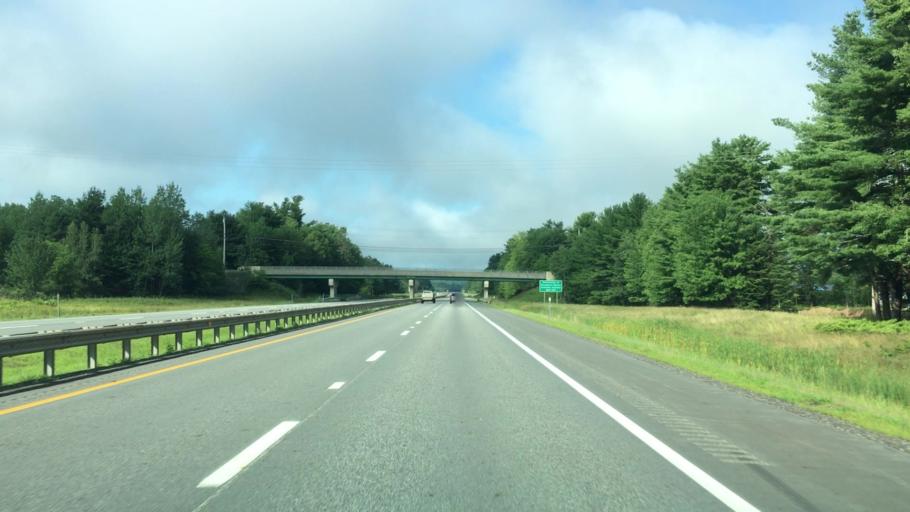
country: US
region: Maine
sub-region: Androscoggin County
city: Sabattus
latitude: 44.0793
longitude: -70.1198
